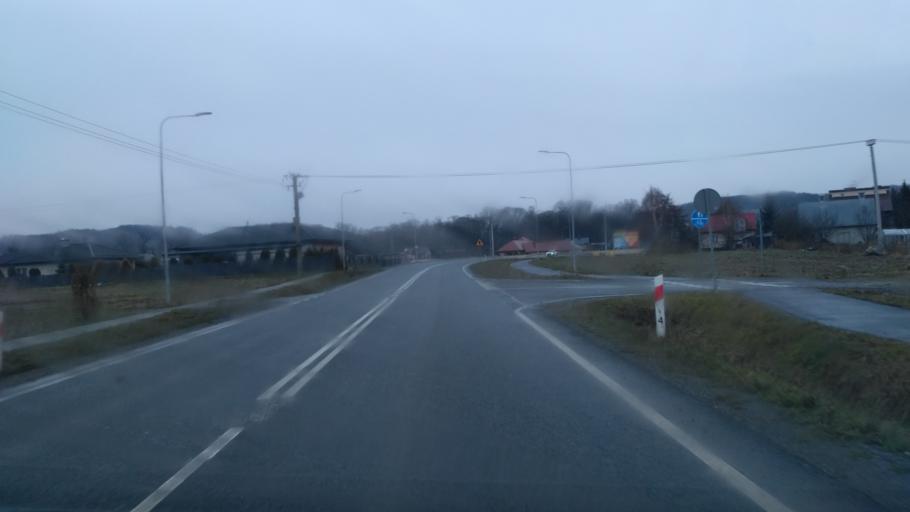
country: PL
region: Subcarpathian Voivodeship
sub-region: Powiat debicki
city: Brzeznica
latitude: 50.0630
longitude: 21.4767
